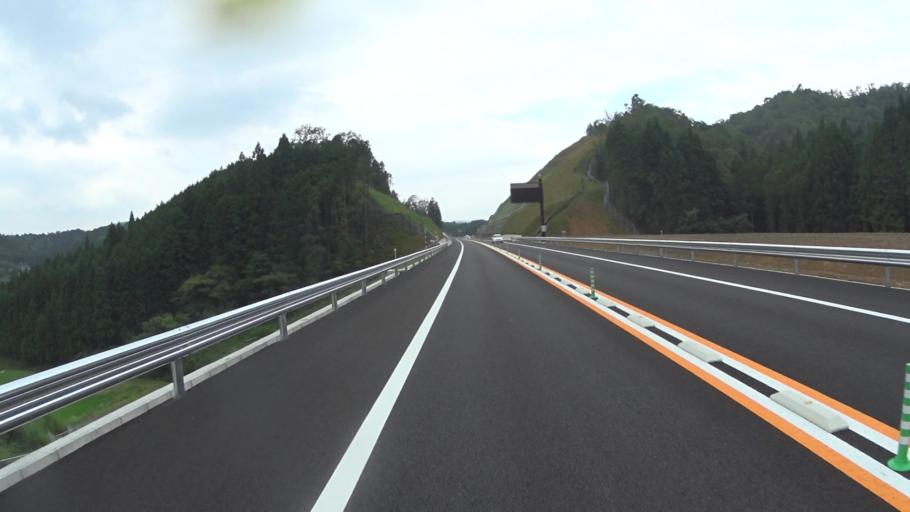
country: JP
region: Kyoto
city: Ayabe
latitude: 35.2032
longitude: 135.3513
